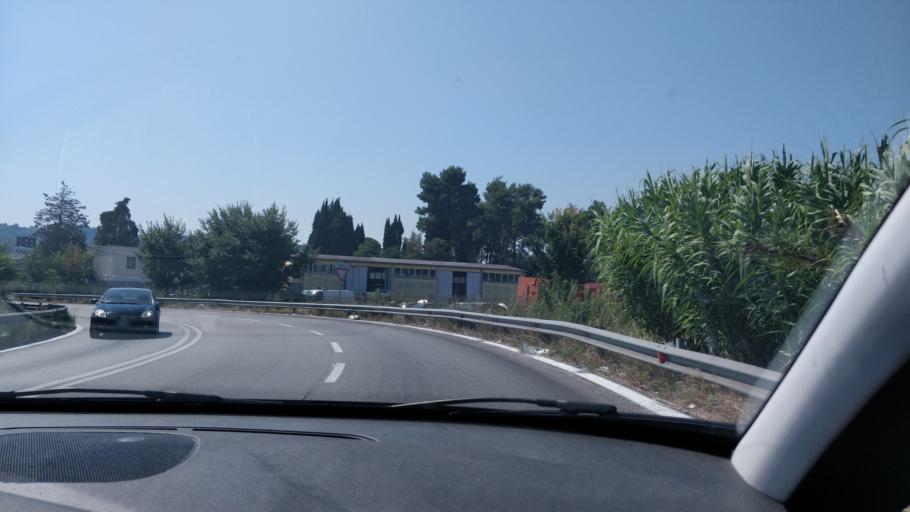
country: IT
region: Abruzzo
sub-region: Provincia di Pescara
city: Villa Raspa
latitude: 42.4398
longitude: 14.1942
